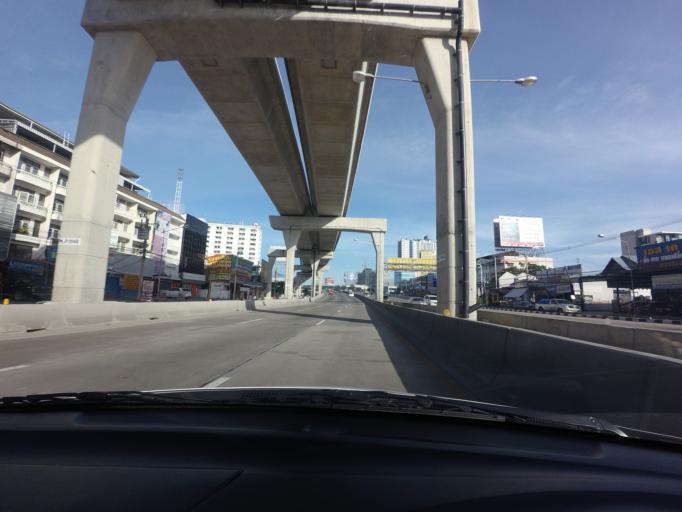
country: TH
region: Nonthaburi
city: Mueang Nonthaburi
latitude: 13.8699
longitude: 100.4863
